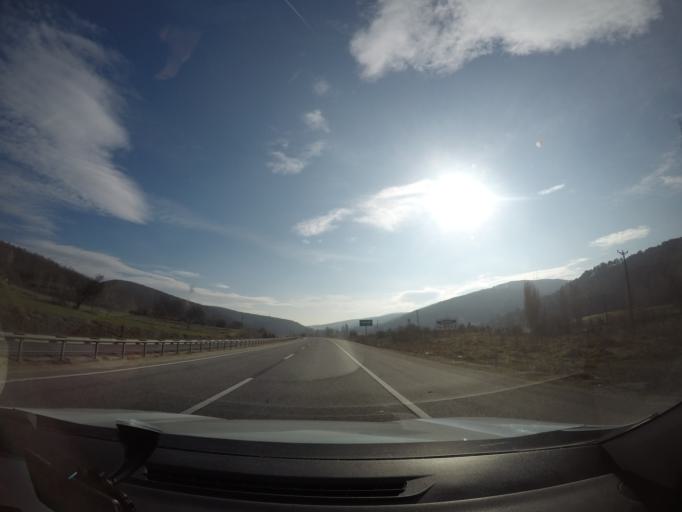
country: TR
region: Bilecik
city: Dodurga
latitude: 39.8902
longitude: 29.9118
